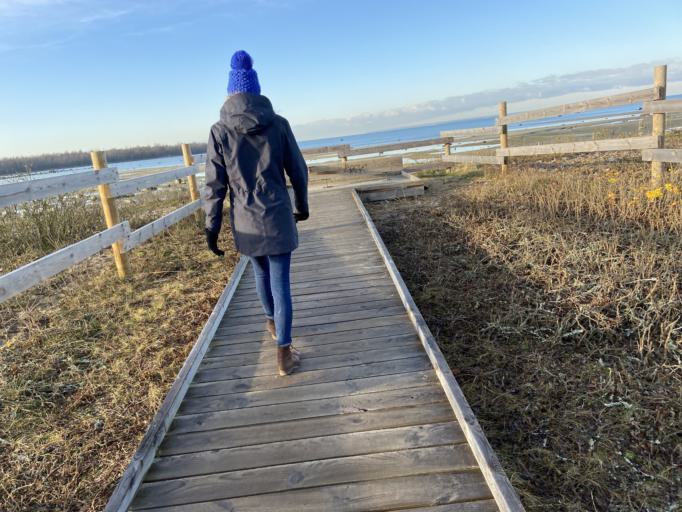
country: EE
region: Harju
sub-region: Tallinna linn
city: Tallinn
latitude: 59.4826
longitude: 24.7078
